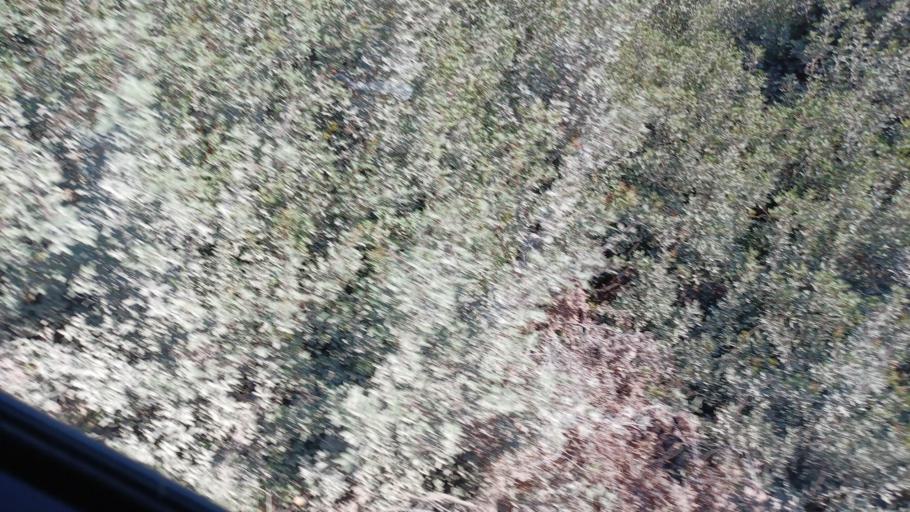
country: CY
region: Limassol
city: Pissouri
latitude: 34.7110
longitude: 32.6805
